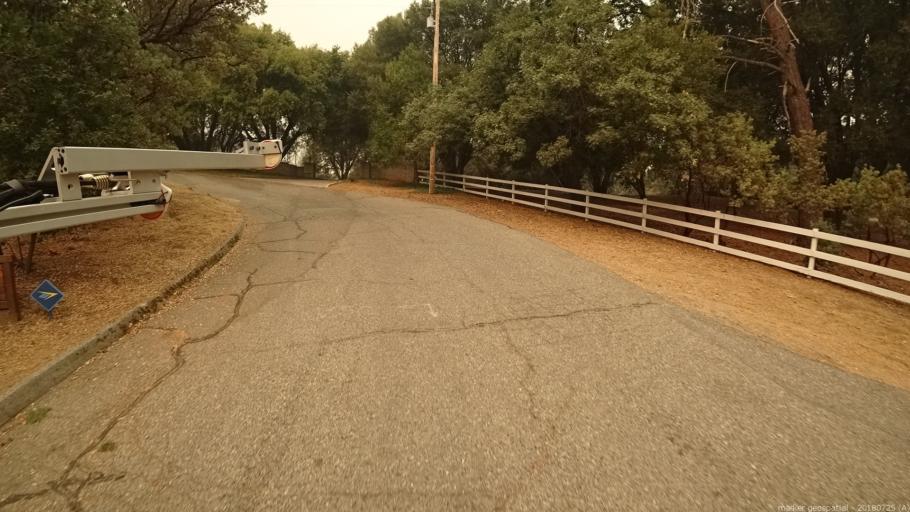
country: US
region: California
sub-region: Madera County
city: Oakhurst
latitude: 37.3570
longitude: -119.6155
